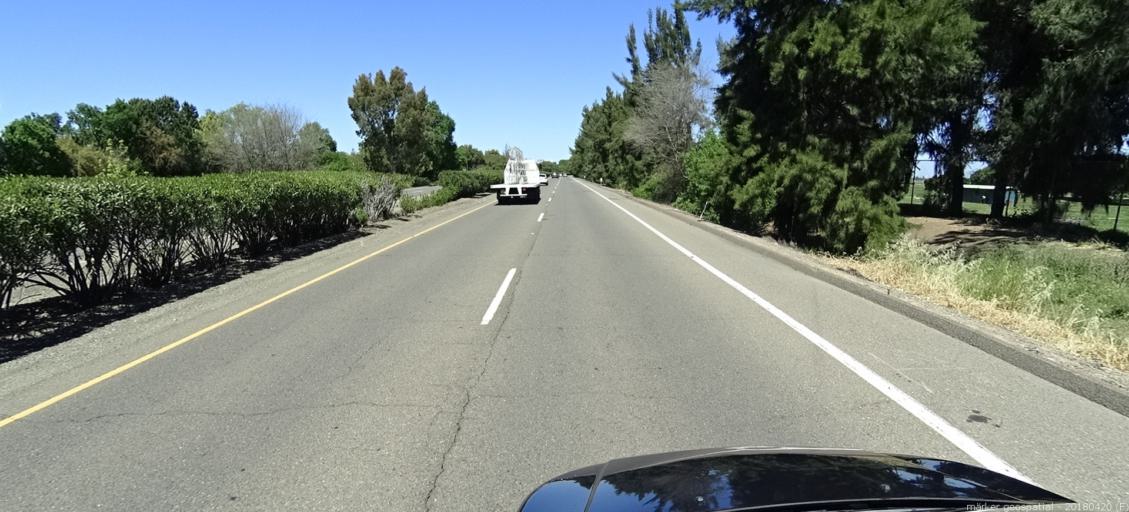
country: US
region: California
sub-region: Sacramento County
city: Parkway
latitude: 38.4992
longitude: -121.5059
